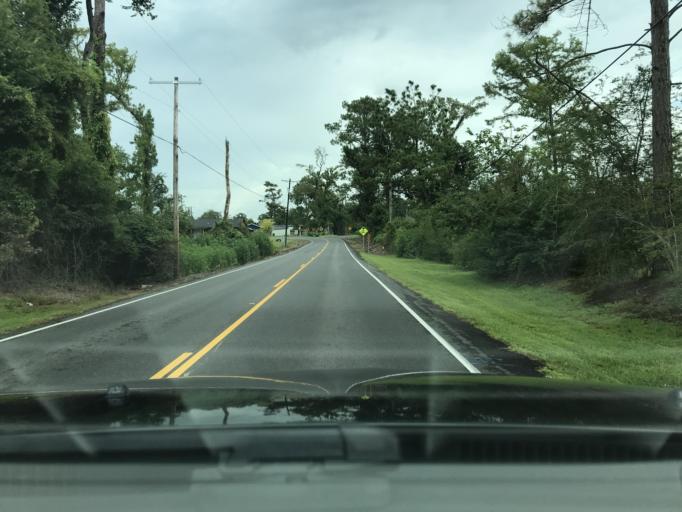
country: US
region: Louisiana
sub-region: Calcasieu Parish
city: Moss Bluff
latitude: 30.3008
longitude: -93.1839
